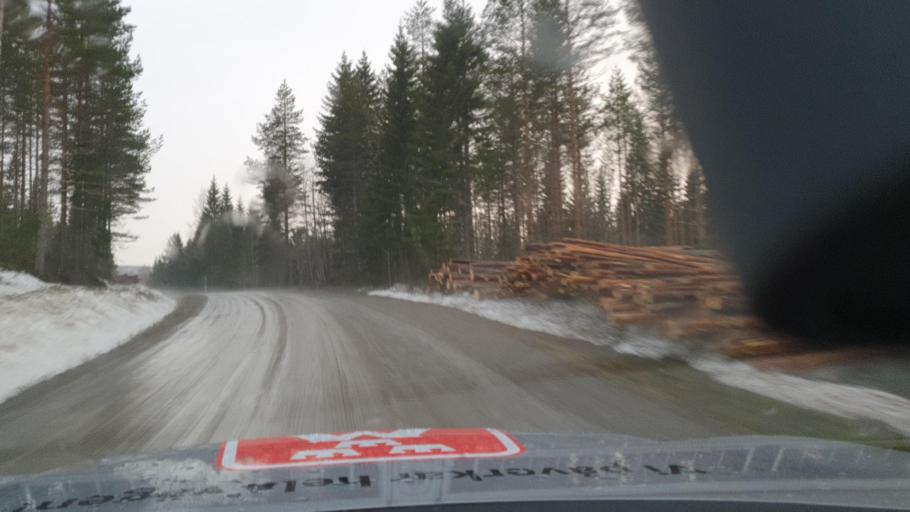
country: SE
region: Vaesternorrland
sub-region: OErnskoeldsviks Kommun
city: Bjasta
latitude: 63.2116
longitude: 18.3389
